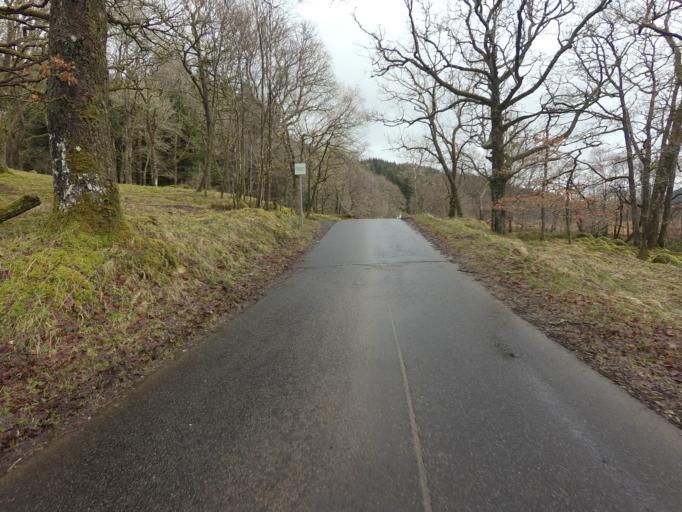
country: GB
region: Scotland
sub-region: West Dunbartonshire
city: Balloch
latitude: 56.2198
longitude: -4.5482
